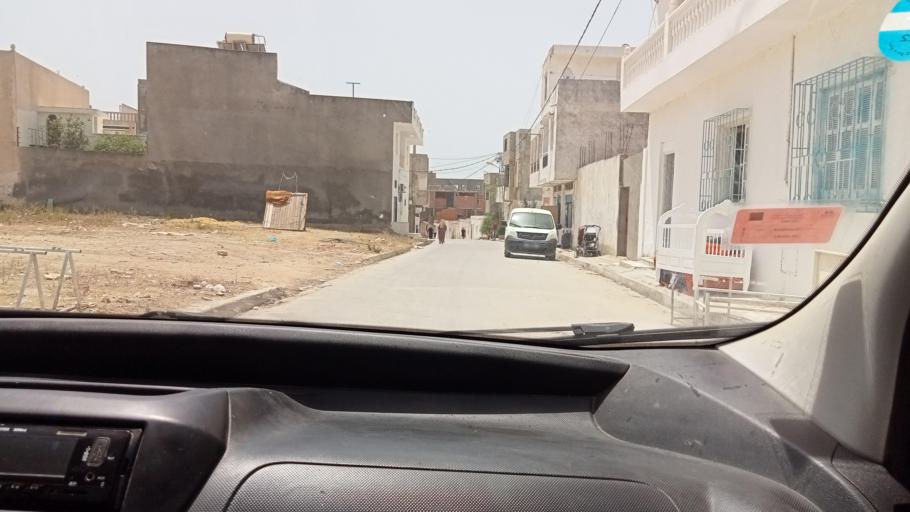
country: TN
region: Nabul
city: Qulaybiyah
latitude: 36.8538
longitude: 11.0885
